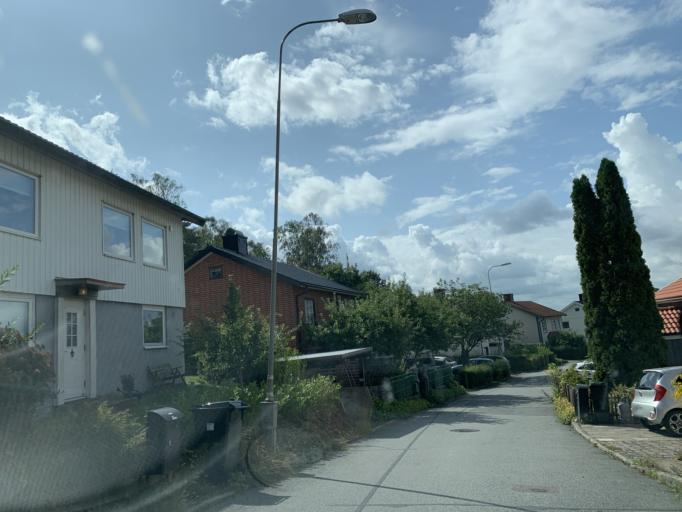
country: SE
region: Vaestra Goetaland
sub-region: Goteborg
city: Eriksbo
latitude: 57.7471
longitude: 12.0528
